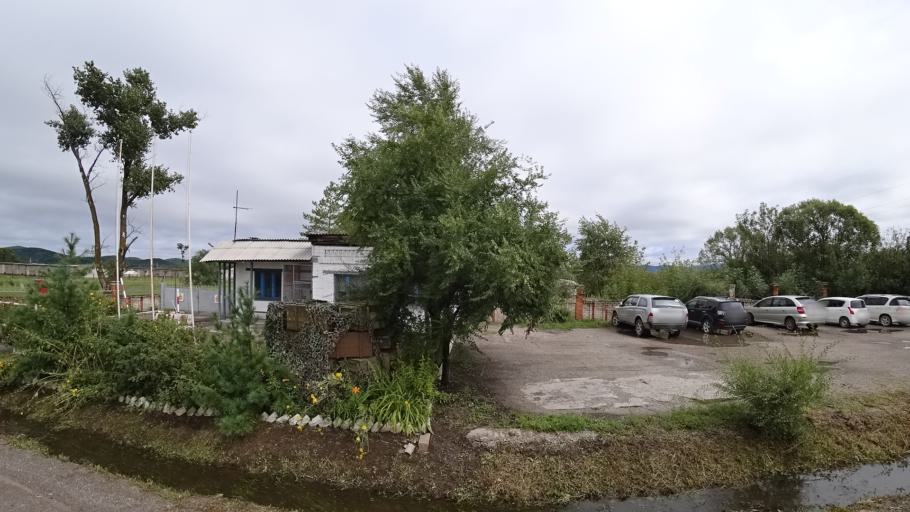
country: RU
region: Primorskiy
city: Monastyrishche
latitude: 44.2019
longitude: 132.4756
